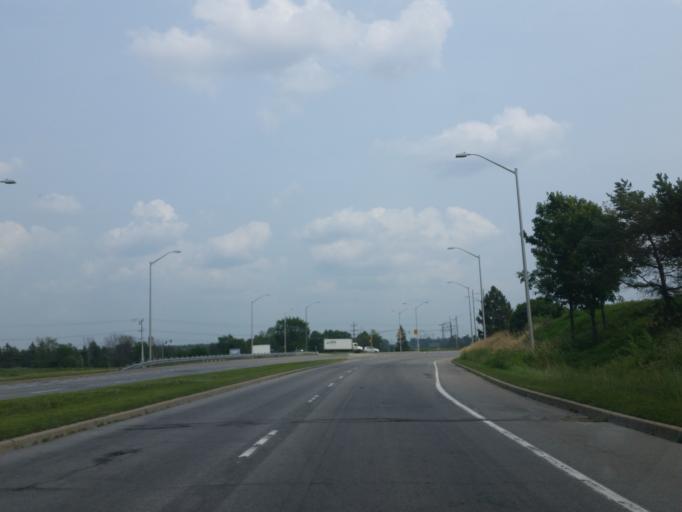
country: CA
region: Ontario
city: Bells Corners
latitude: 45.3327
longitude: -75.8959
